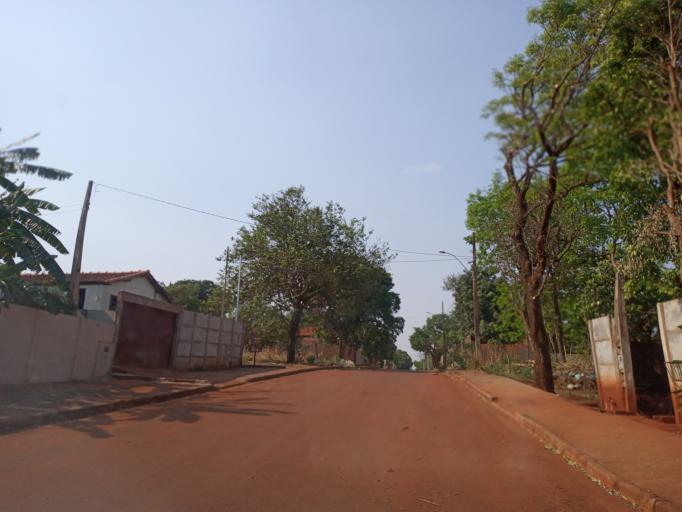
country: BR
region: Minas Gerais
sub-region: Ituiutaba
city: Ituiutaba
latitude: -18.9616
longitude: -49.4771
